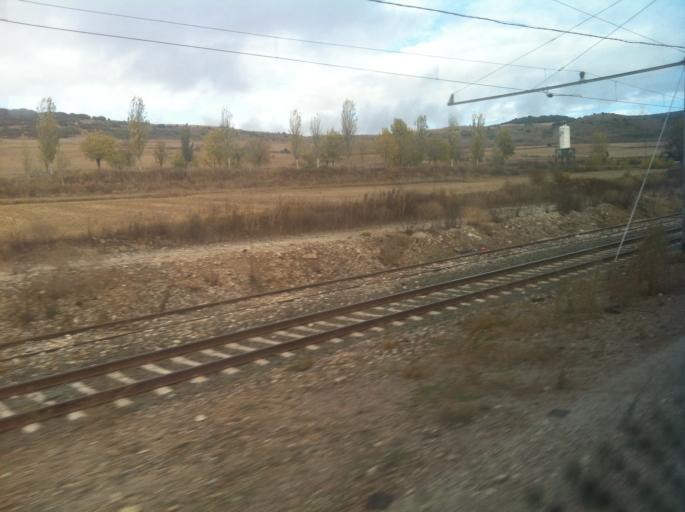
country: ES
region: Castille and Leon
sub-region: Provincia de Burgos
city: Santa Olalla de Bureba
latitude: 42.4656
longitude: -3.4469
